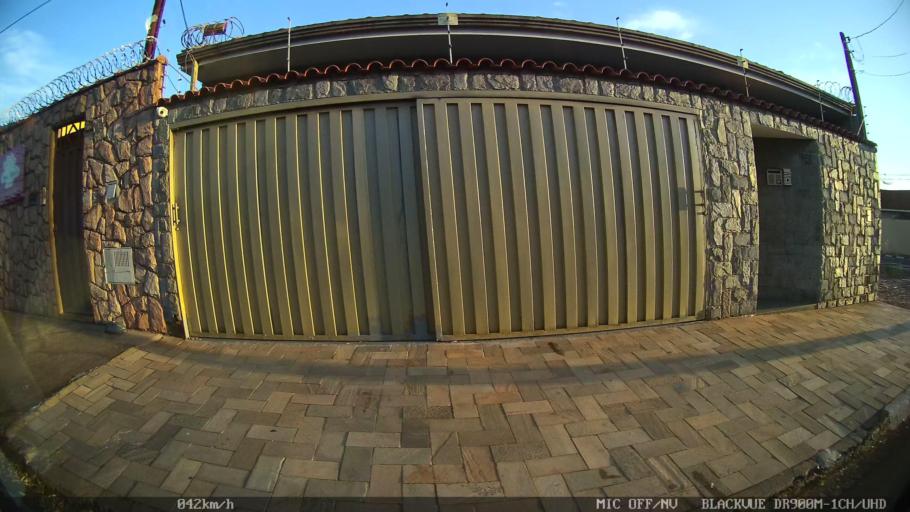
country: BR
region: Sao Paulo
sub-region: Franca
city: Franca
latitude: -20.5182
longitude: -47.4093
